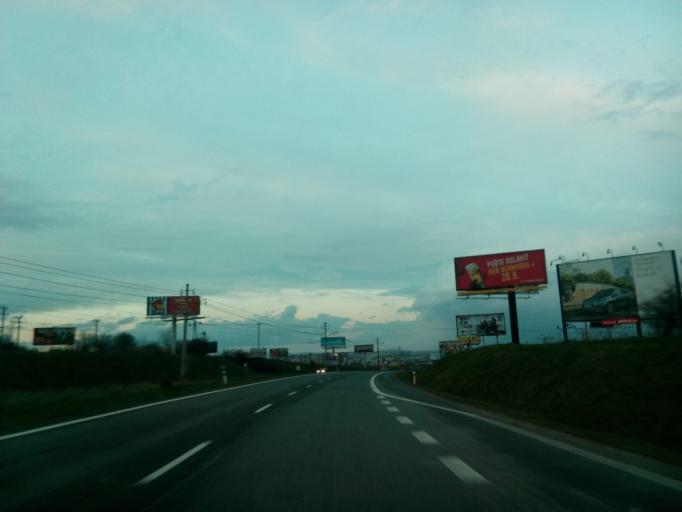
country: SK
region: Kosicky
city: Kosice
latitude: 48.6884
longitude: 21.2249
